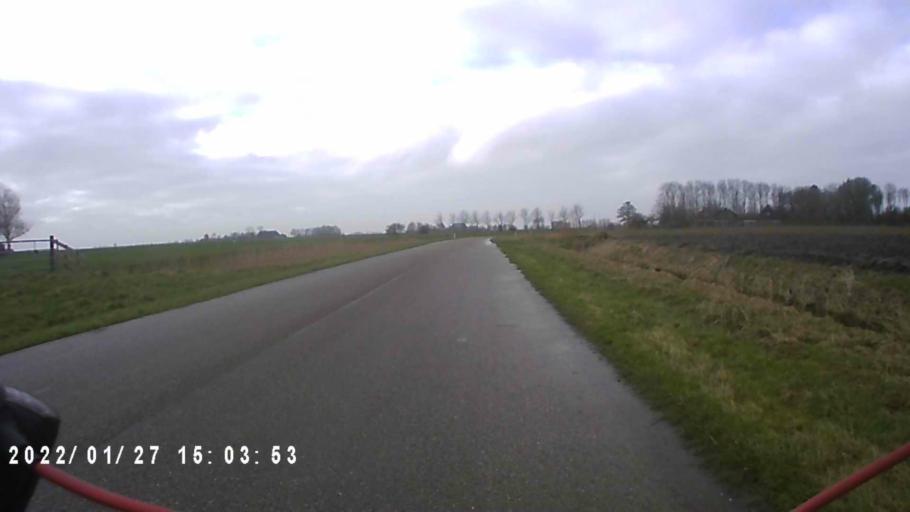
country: NL
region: Friesland
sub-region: Gemeente Dongeradeel
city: Anjum
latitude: 53.3705
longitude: 6.1464
